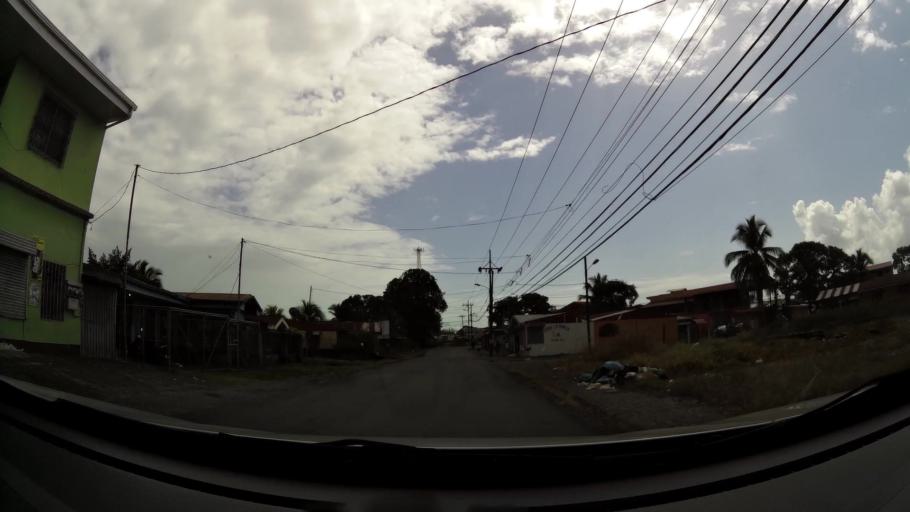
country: CR
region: Limon
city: Limon
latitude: 9.9864
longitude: -83.0473
